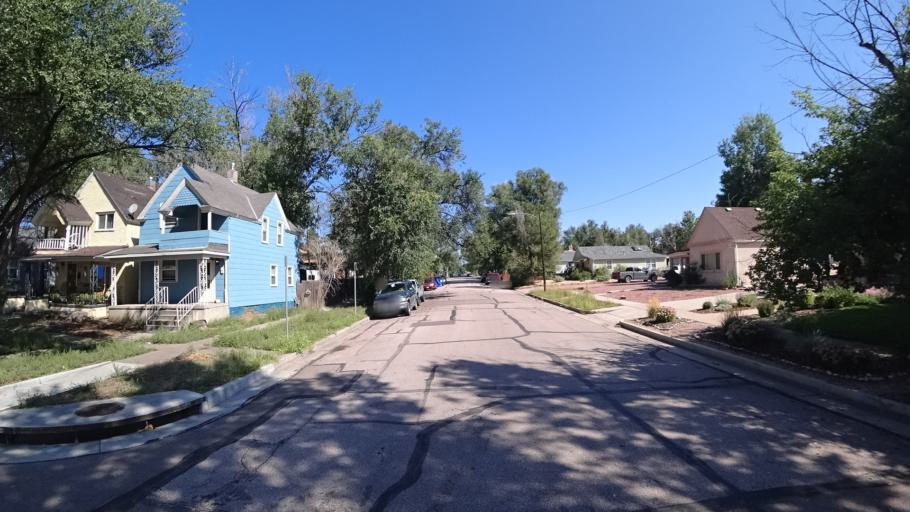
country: US
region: Colorado
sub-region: El Paso County
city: Colorado Springs
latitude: 38.8449
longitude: -104.8126
